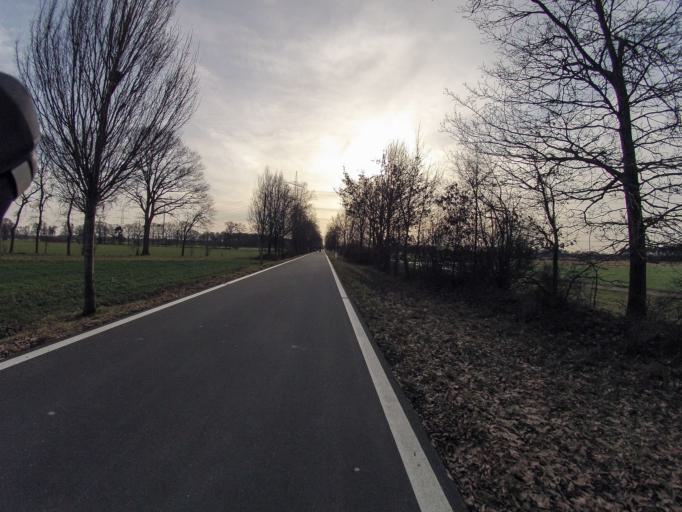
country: DE
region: North Rhine-Westphalia
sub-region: Regierungsbezirk Munster
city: Neuenkirchen
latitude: 52.1900
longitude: 7.3787
